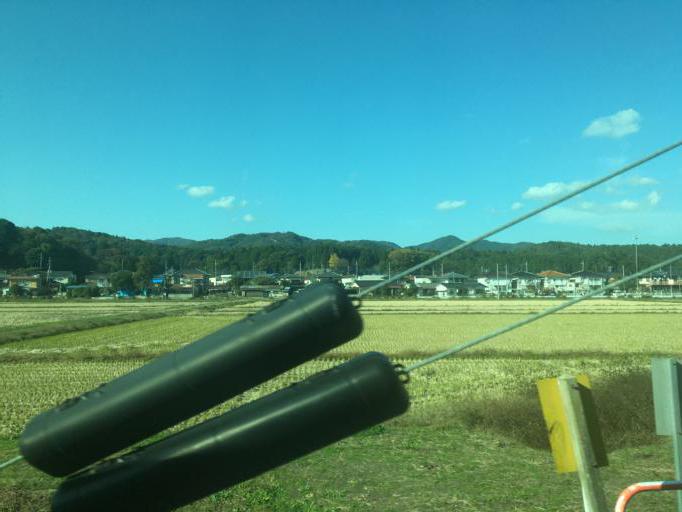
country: JP
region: Ibaraki
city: Kasama
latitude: 36.3670
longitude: 140.2115
